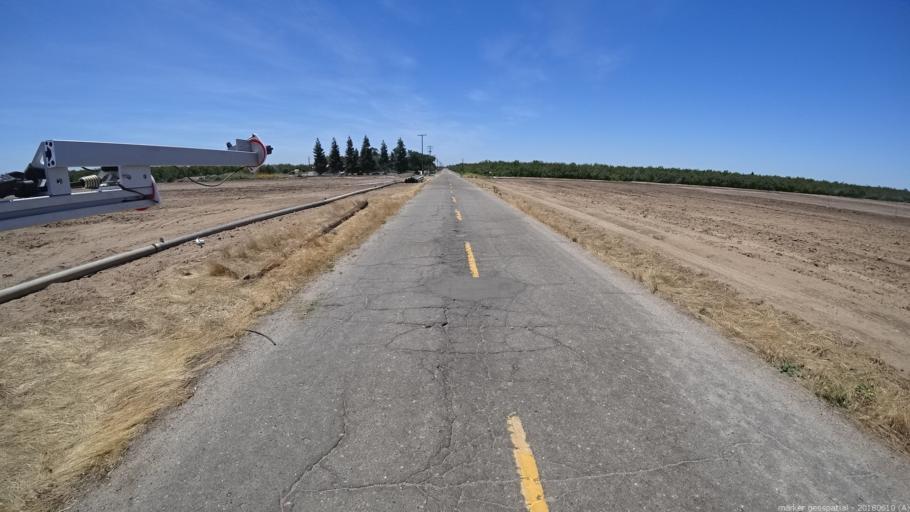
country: US
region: California
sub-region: Madera County
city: Chowchilla
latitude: 37.0765
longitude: -120.2603
